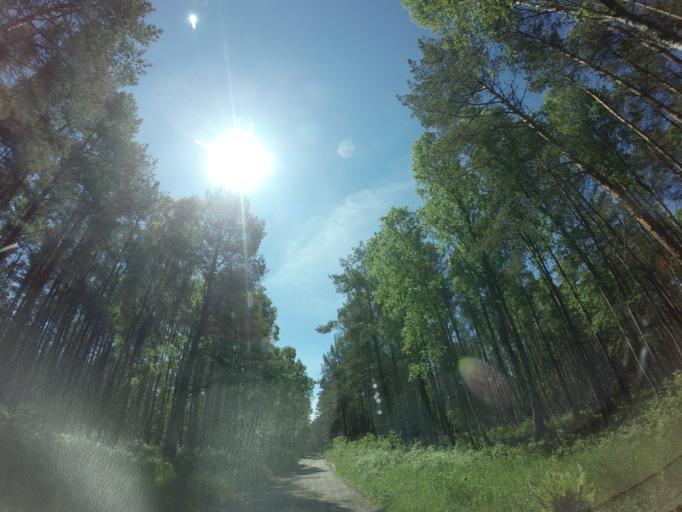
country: PL
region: West Pomeranian Voivodeship
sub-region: Powiat choszczenski
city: Drawno
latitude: 53.3076
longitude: 15.6899
